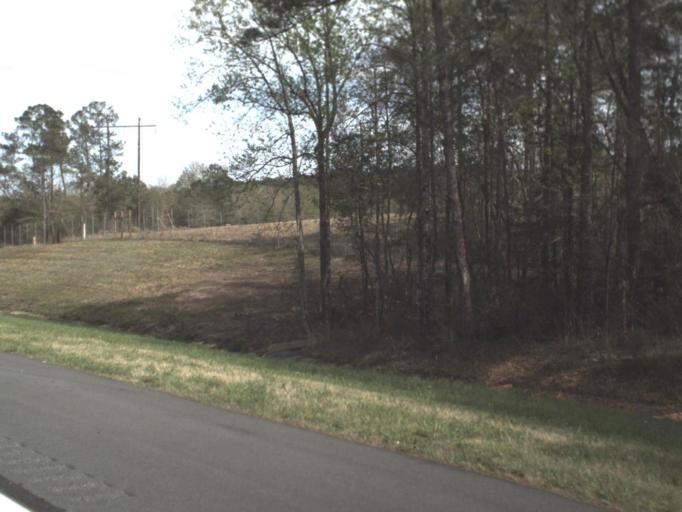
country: US
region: Florida
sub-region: Walton County
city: DeFuniak Springs
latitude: 30.6982
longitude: -85.9794
